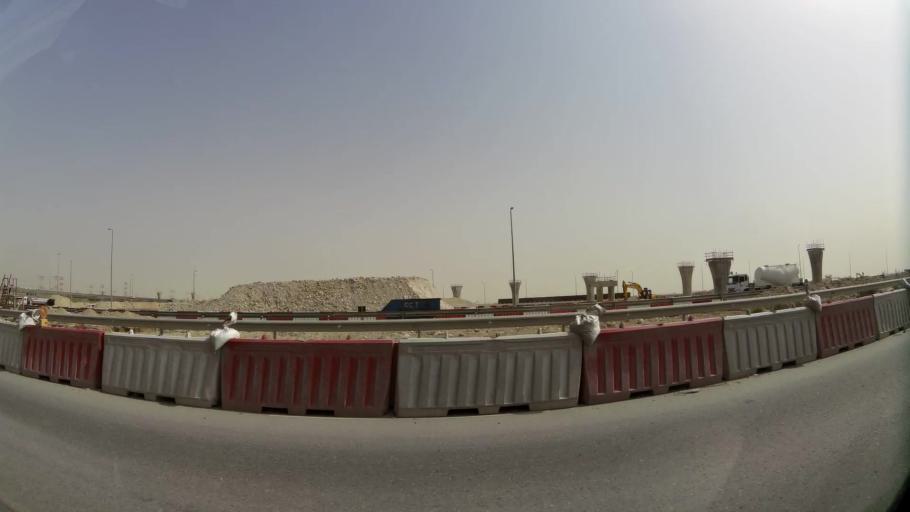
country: QA
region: Baladiyat ar Rayyan
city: Ar Rayyan
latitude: 25.1719
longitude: 51.3249
